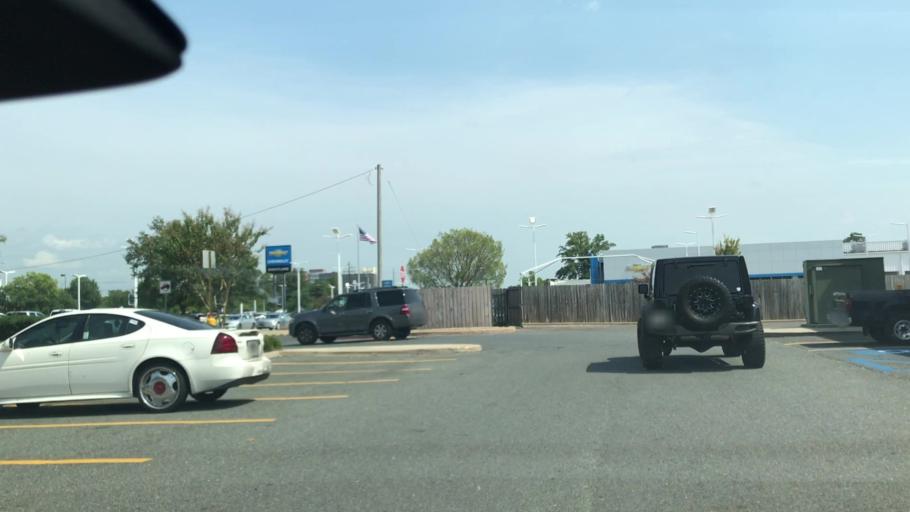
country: US
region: Louisiana
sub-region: Bossier Parish
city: Bossier City
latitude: 32.4374
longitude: -93.7162
